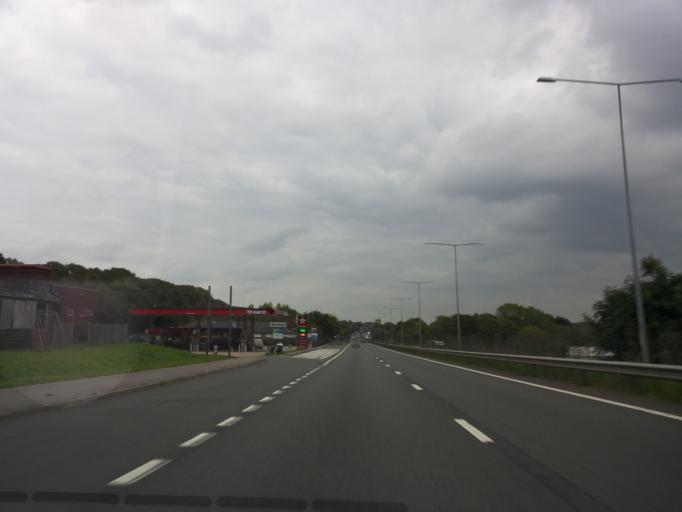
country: GB
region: England
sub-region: Kent
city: Dunkirk
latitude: 51.2878
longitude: 1.0099
